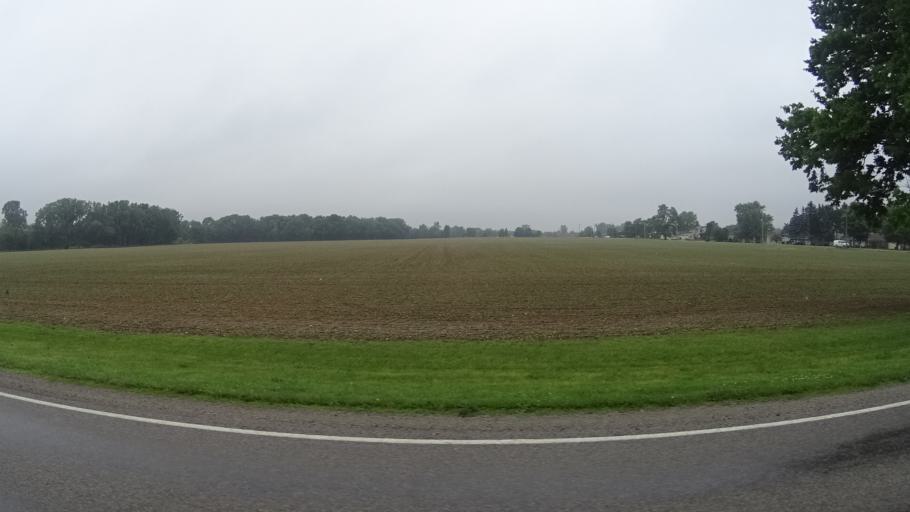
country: US
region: Ohio
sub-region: Huron County
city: Bellevue
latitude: 41.3618
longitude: -82.7878
